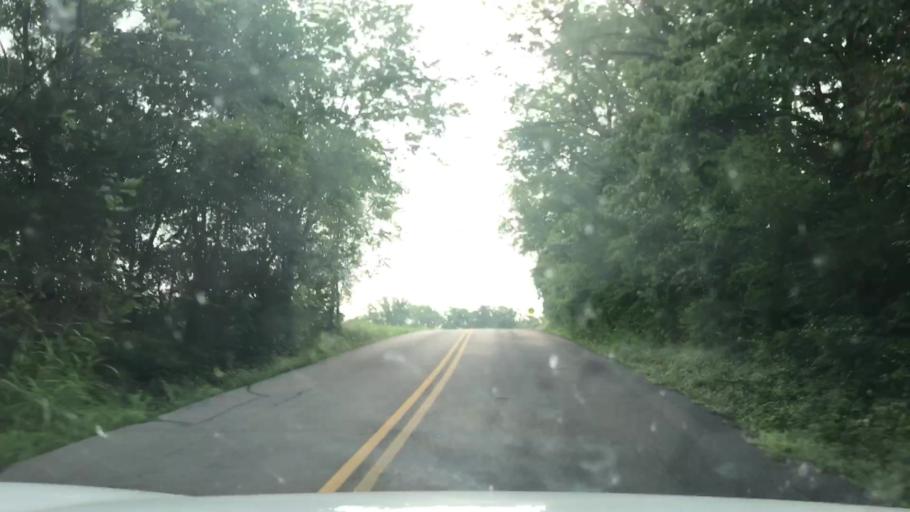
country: US
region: Missouri
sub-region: Saint Charles County
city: Cottleville
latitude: 38.7045
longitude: -90.6447
